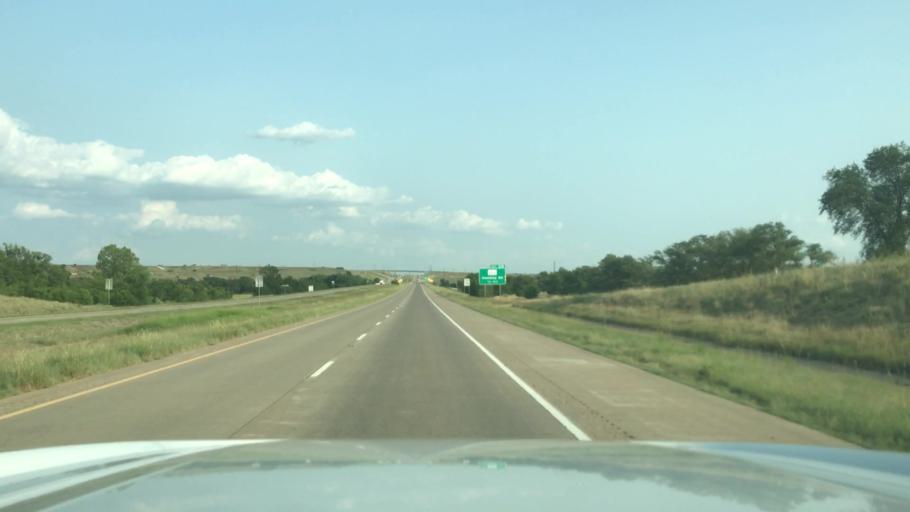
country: US
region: Texas
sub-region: Randall County
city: Canyon
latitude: 35.0110
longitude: -101.9083
